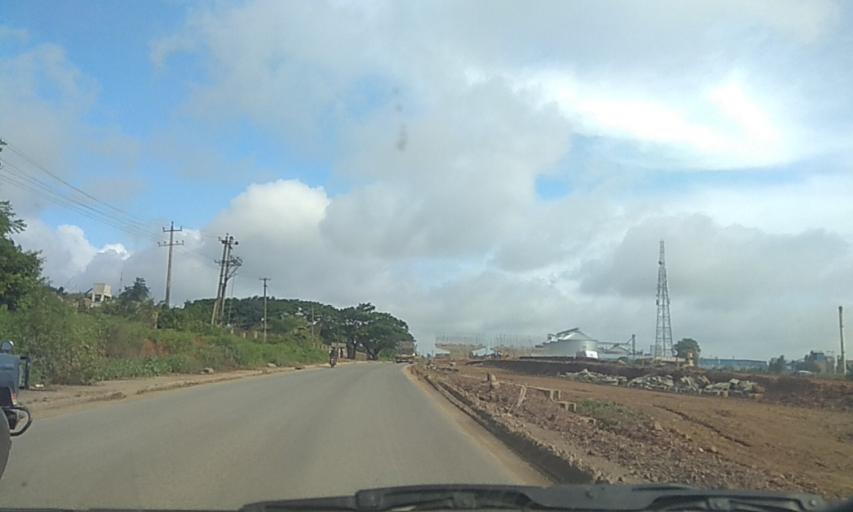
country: IN
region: Karnataka
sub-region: Haveri
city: Shiggaon
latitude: 15.0381
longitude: 75.1726
